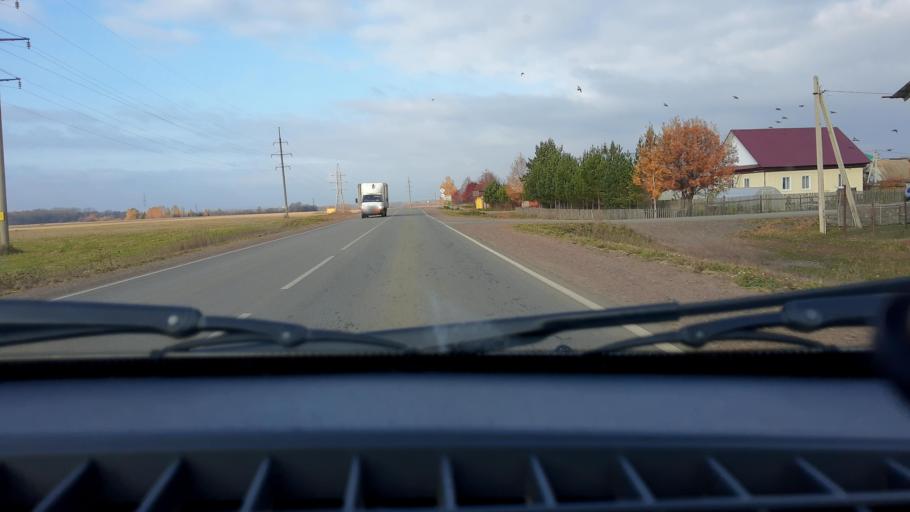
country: RU
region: Bashkortostan
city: Kabakovo
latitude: 54.5467
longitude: 56.0385
